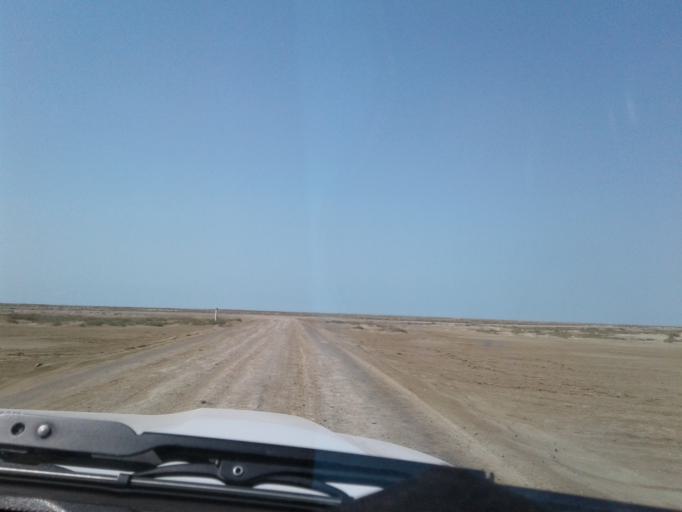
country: IR
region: Golestan
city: Gomishan
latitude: 37.8357
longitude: 53.9105
